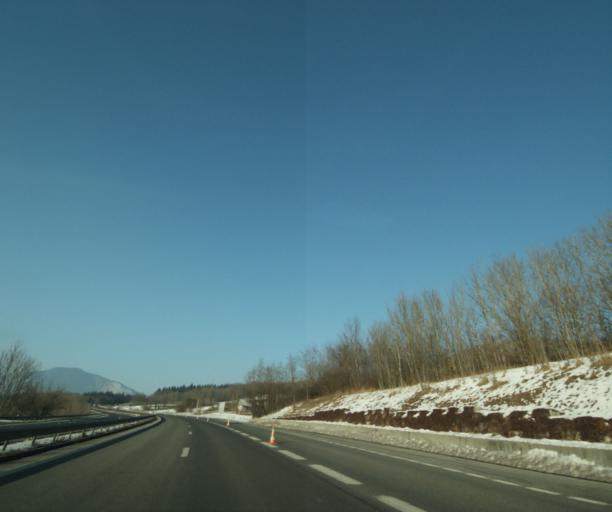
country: FR
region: Rhone-Alpes
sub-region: Departement de la Haute-Savoie
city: Frangy
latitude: 46.0651
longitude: 5.9045
